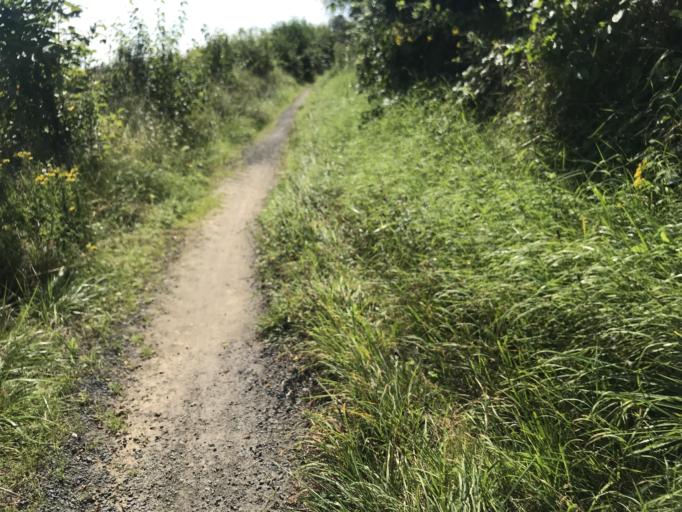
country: DE
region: Hesse
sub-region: Regierungsbezirk Giessen
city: Hungen
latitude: 50.4401
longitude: 8.8905
